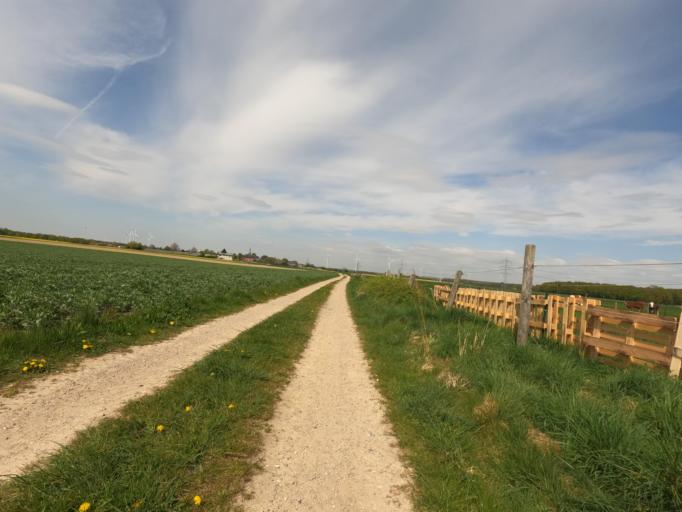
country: DE
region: North Rhine-Westphalia
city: Geilenkirchen
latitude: 50.9884
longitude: 6.1262
